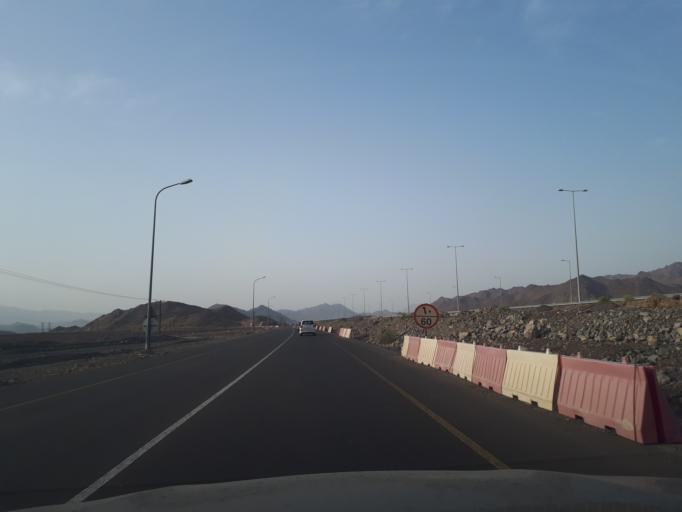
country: OM
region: Muhafazat ad Dakhiliyah
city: Sufalat Sama'il
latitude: 23.2795
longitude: 58.1071
